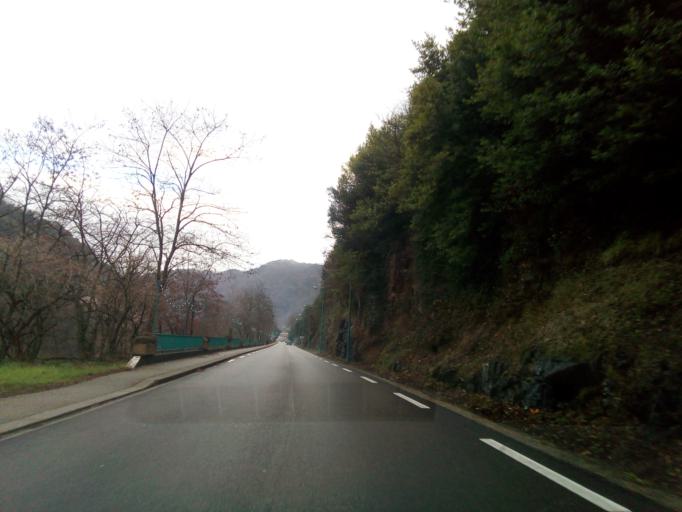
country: FR
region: Rhone-Alpes
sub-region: Departement de l'Ardeche
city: Saint-Sauveur-de-Montagut
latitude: 44.8200
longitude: 4.5886
